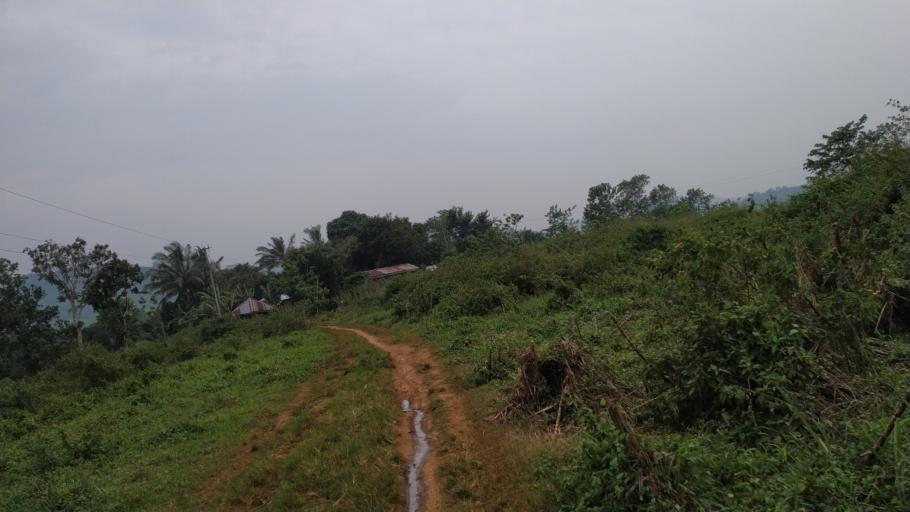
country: PH
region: Western Visayas
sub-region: Province of Negros Occidental
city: Quezon
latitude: 10.4214
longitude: 123.2407
